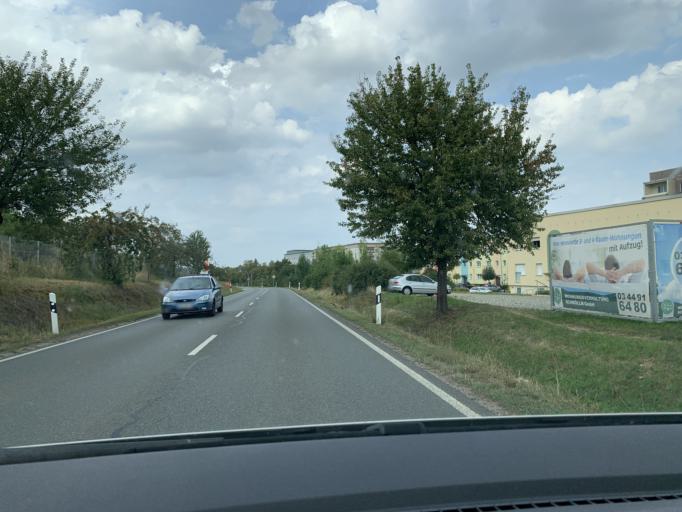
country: DE
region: Thuringia
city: Schmolln
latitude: 50.8843
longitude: 12.3512
